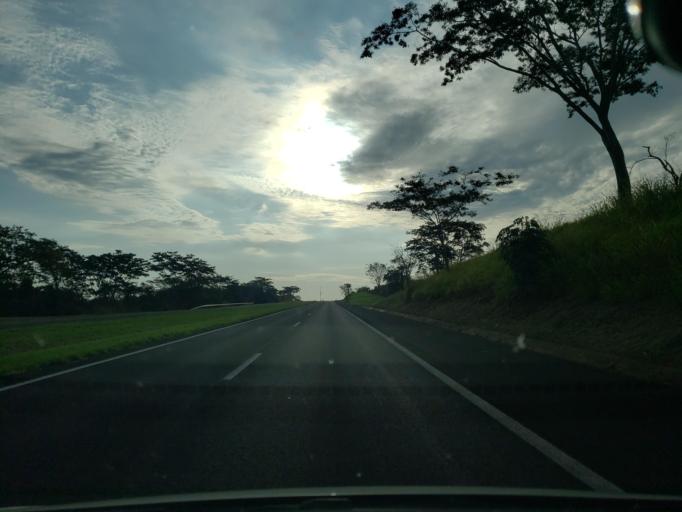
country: BR
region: Sao Paulo
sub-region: Mirandopolis
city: Mirandopolis
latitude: -21.1118
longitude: -51.0223
